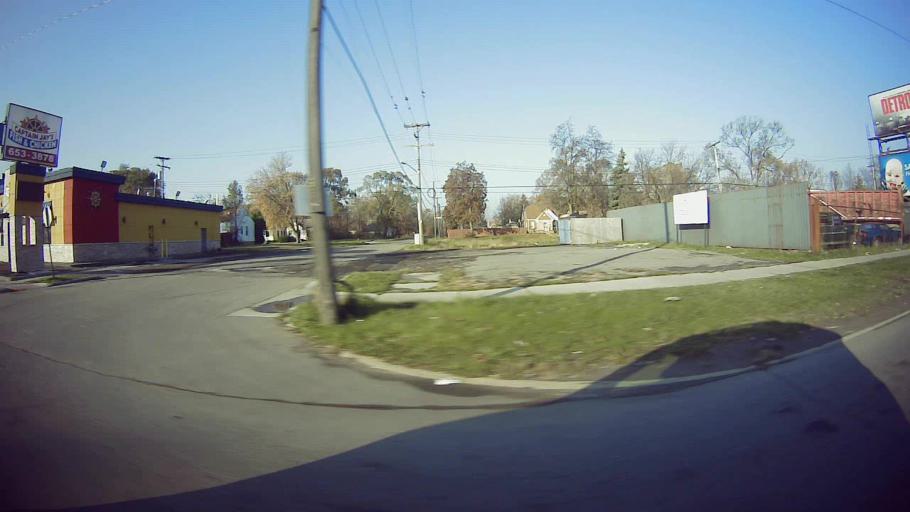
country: US
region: Michigan
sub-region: Wayne County
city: Dearborn
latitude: 42.3636
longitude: -83.1973
